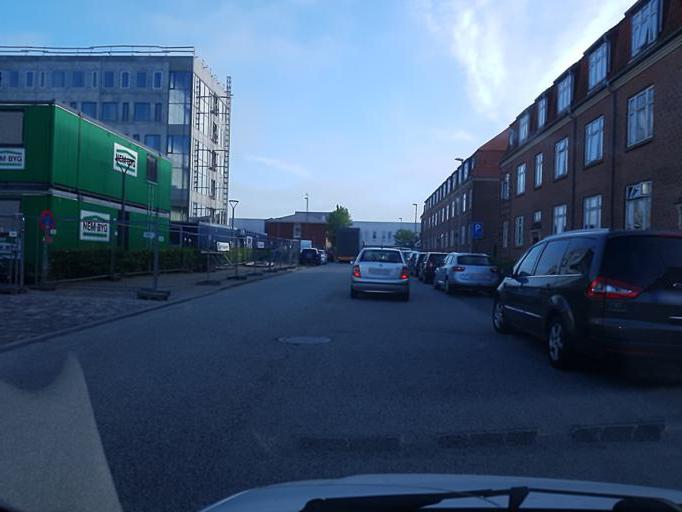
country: DK
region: South Denmark
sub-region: Esbjerg Kommune
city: Esbjerg
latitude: 55.4738
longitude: 8.4589
